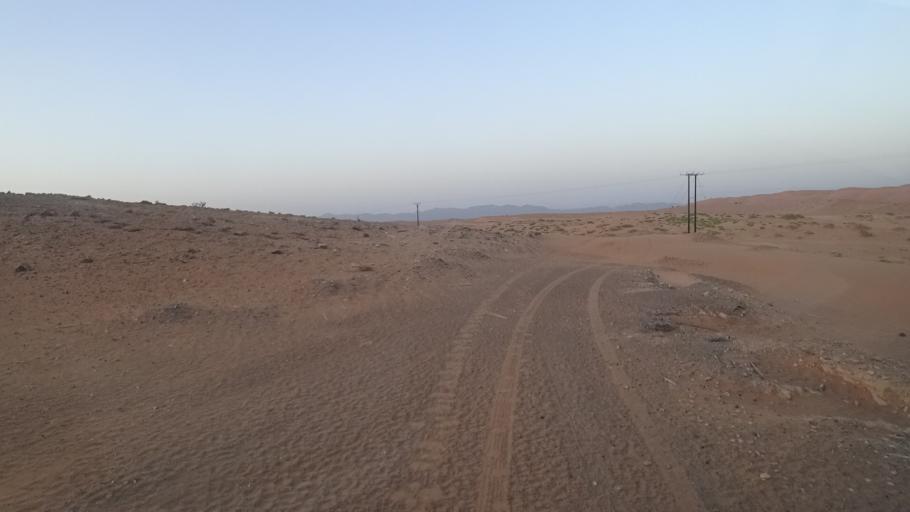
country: OM
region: Ash Sharqiyah
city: Al Qabil
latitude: 22.4826
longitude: 58.7141
